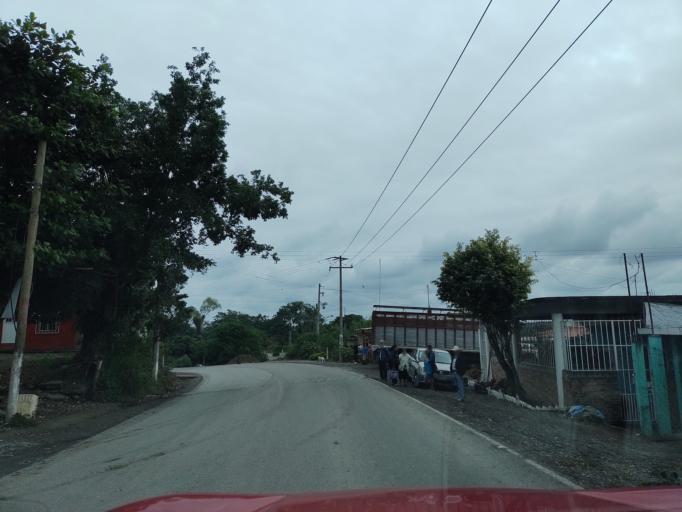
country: MX
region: Puebla
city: Espinal
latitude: 20.2627
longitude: -97.3559
